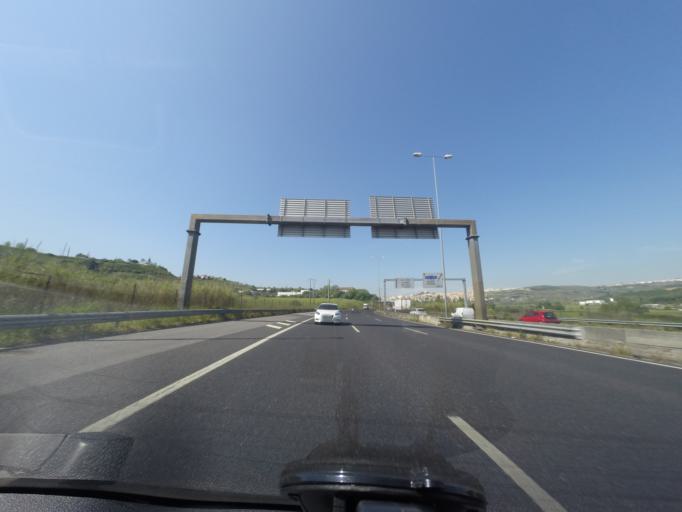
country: PT
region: Lisbon
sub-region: Odivelas
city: Pontinha
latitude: 38.7742
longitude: -9.1972
